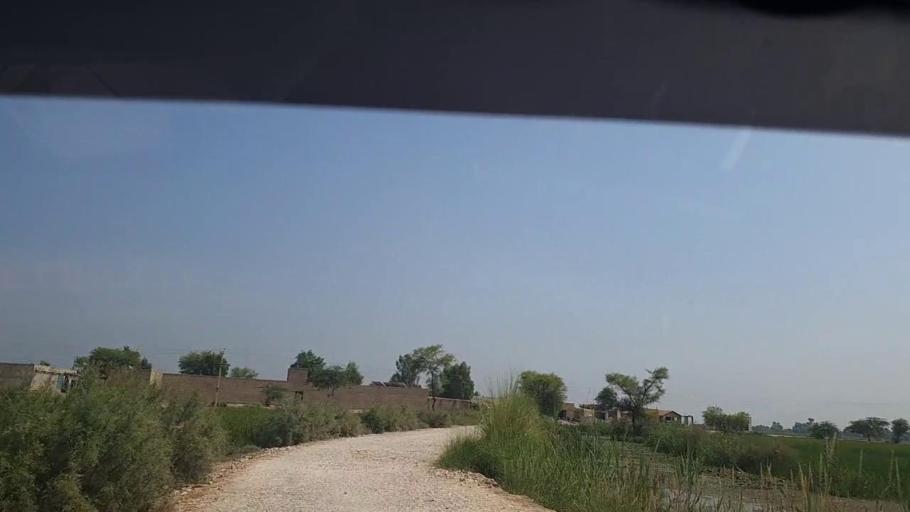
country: PK
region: Sindh
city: Thul
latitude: 28.1945
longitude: 68.7340
